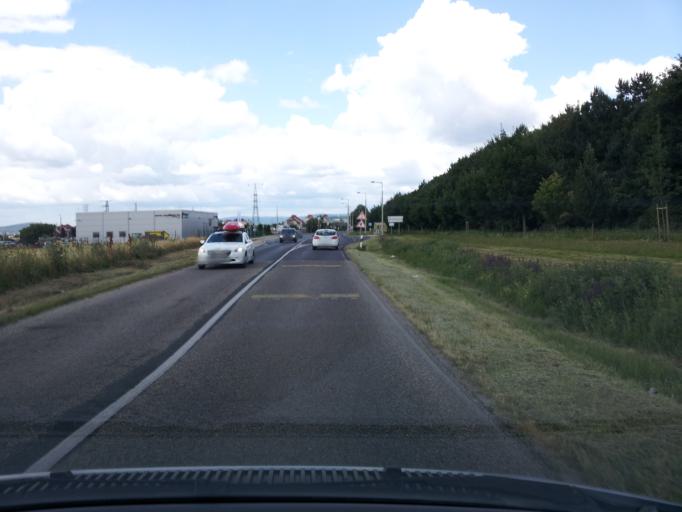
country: HU
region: Veszprem
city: Veszprem
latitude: 47.0788
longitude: 17.9274
